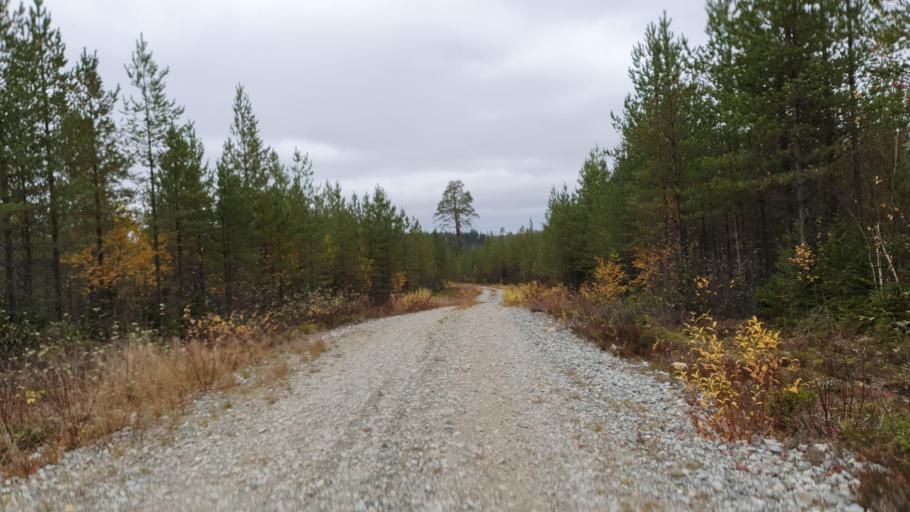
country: FI
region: Kainuu
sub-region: Kehys-Kainuu
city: Kuhmo
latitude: 64.4487
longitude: 29.5995
